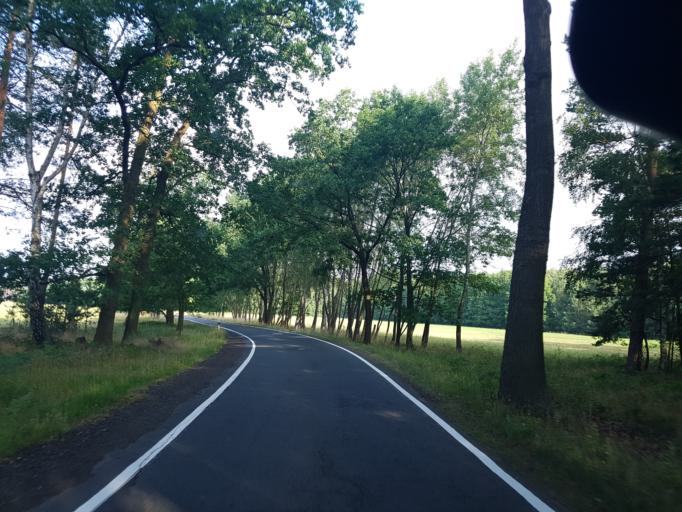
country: DE
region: Saxony-Anhalt
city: Holzdorf
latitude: 51.8578
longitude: 13.0657
